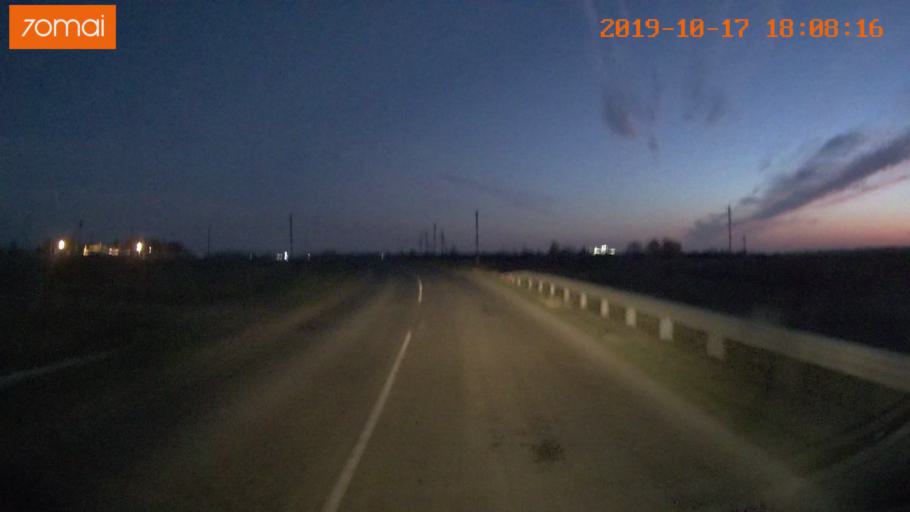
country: RU
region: Tula
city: Kurkino
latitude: 53.4360
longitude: 38.6435
